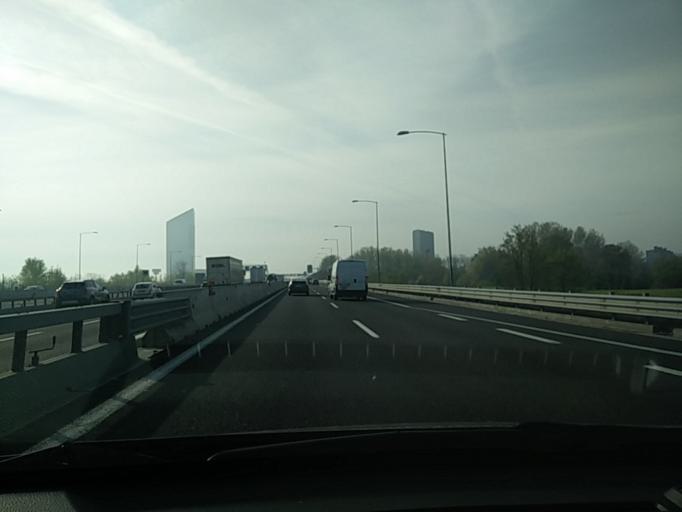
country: IT
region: Emilia-Romagna
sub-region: Provincia di Bologna
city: Quarto Inferiore
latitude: 44.5019
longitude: 11.3835
